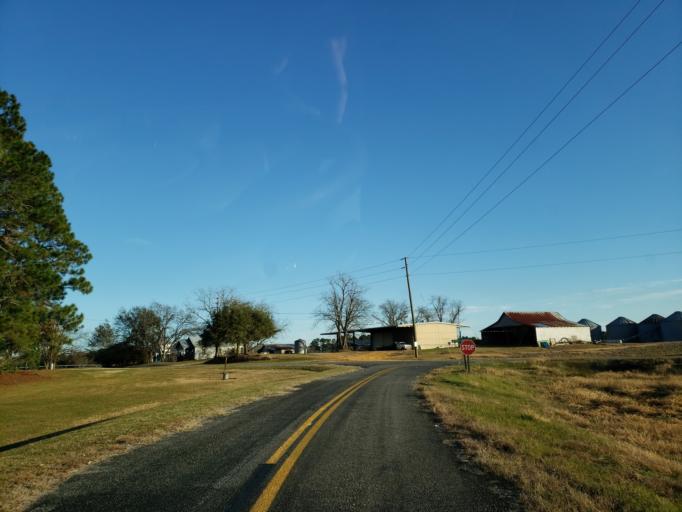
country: US
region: Georgia
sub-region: Dooly County
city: Unadilla
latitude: 32.1876
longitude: -83.7757
